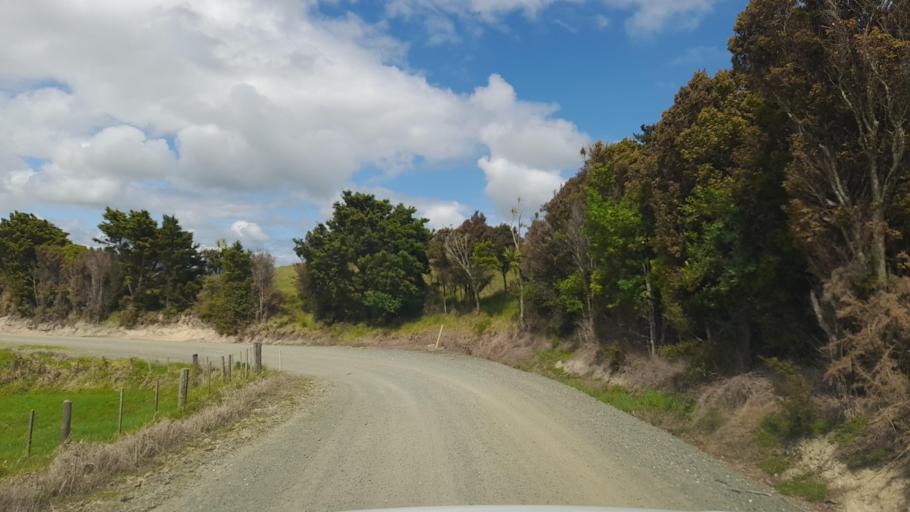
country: NZ
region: Auckland
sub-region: Auckland
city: Wellsford
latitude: -36.2022
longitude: 174.3365
